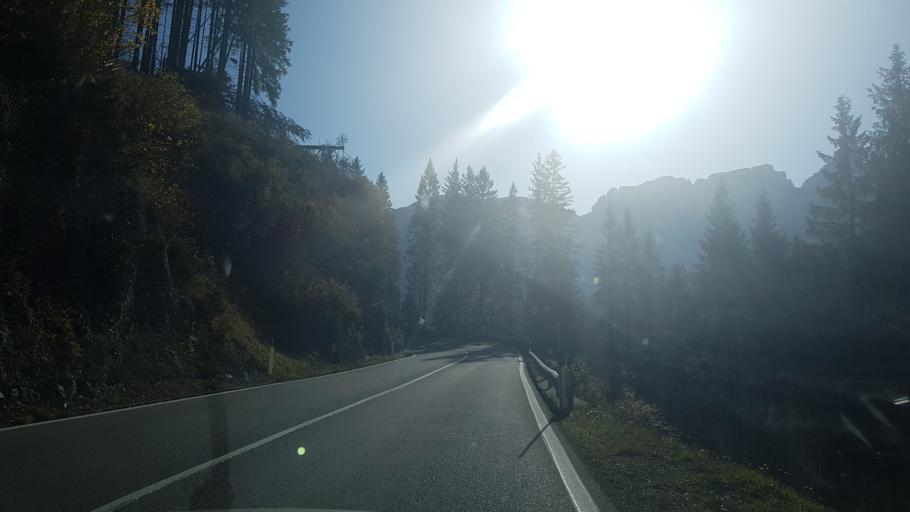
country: IT
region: Veneto
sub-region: Provincia di Belluno
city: Sappada
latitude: 46.5672
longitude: 12.6609
